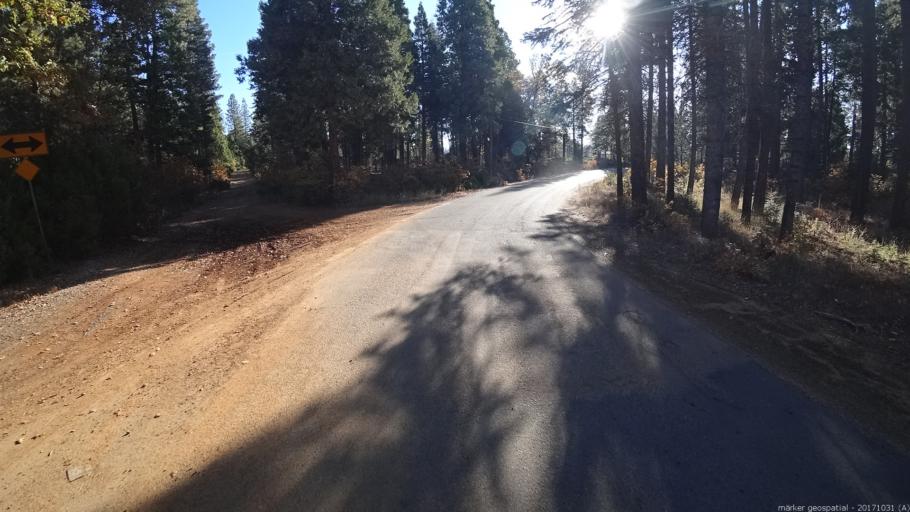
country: US
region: California
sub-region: Shasta County
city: Shingletown
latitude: 40.5180
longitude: -121.8178
